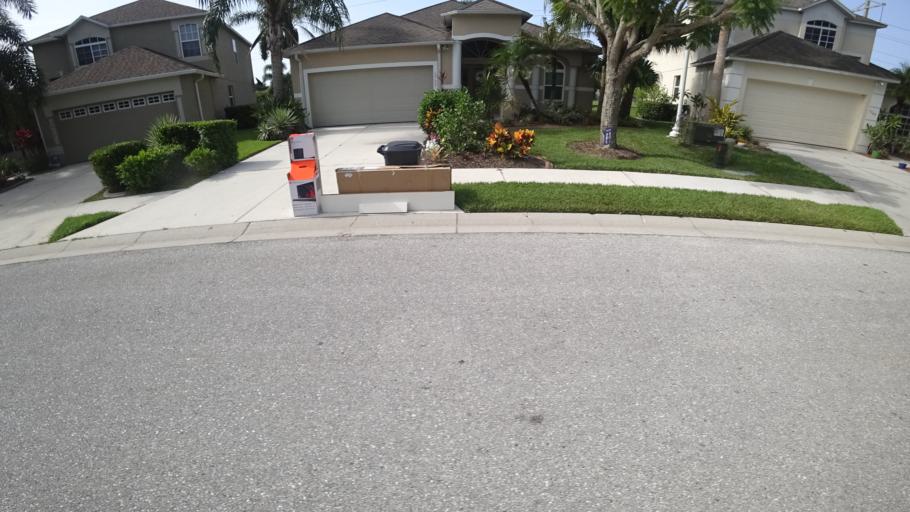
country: US
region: Florida
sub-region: Manatee County
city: Ellenton
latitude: 27.5528
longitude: -82.5045
